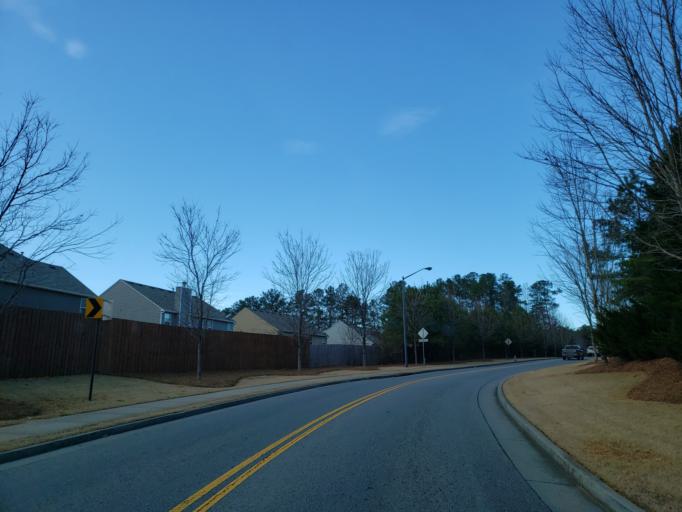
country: US
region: Georgia
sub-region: Cobb County
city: Kennesaw
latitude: 34.0619
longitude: -84.6105
